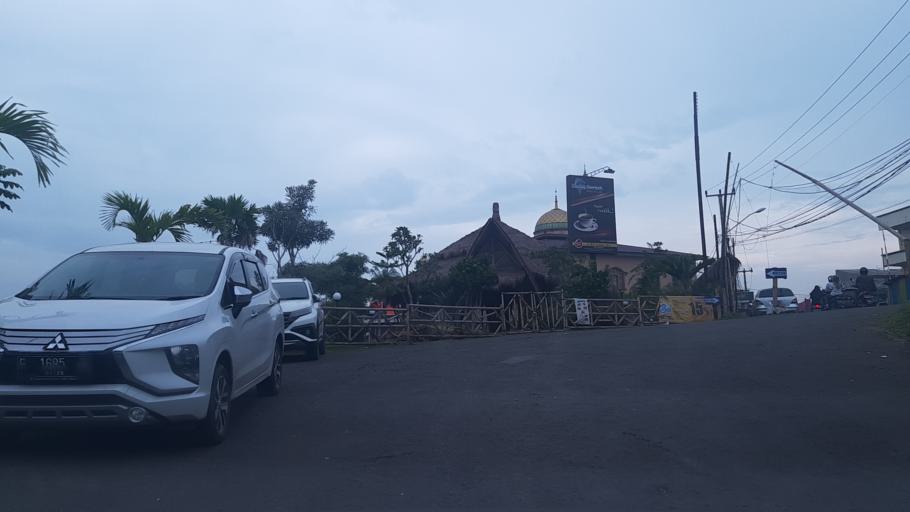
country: ID
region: West Java
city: Cibinong
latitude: -6.4675
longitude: 106.8567
